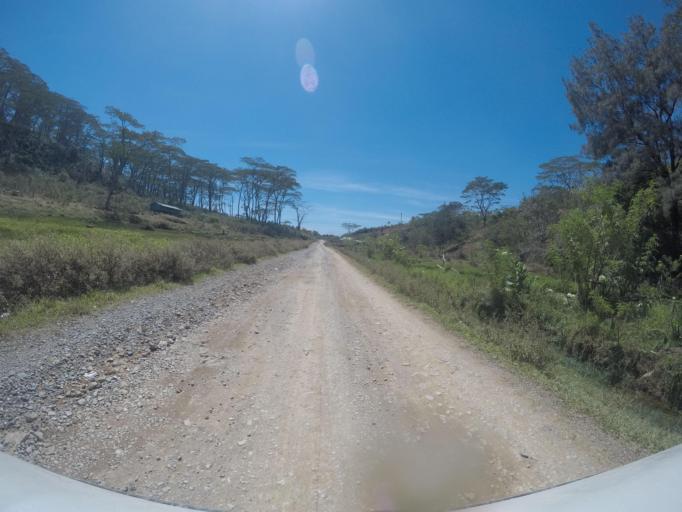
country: TL
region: Ermera
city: Gleno
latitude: -8.7744
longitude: 125.3946
